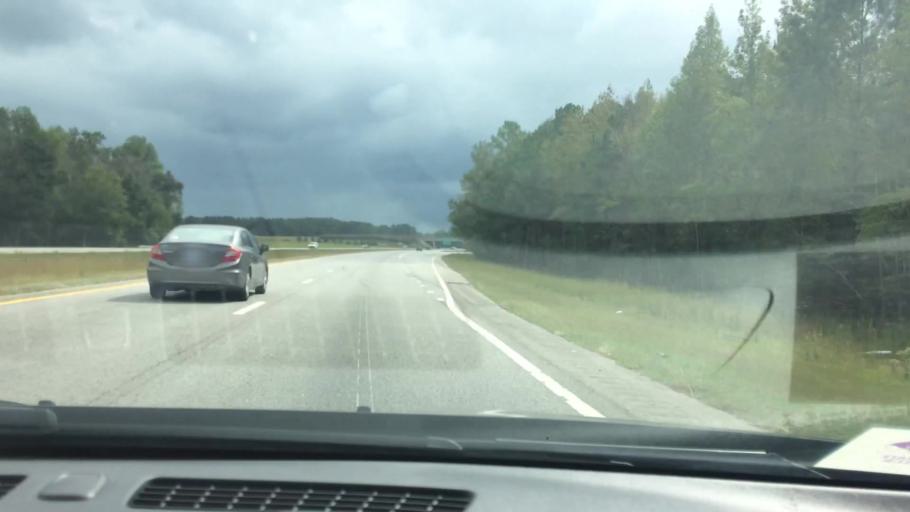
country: US
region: North Carolina
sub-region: Wilson County
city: Lucama
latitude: 35.7660
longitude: -78.0329
